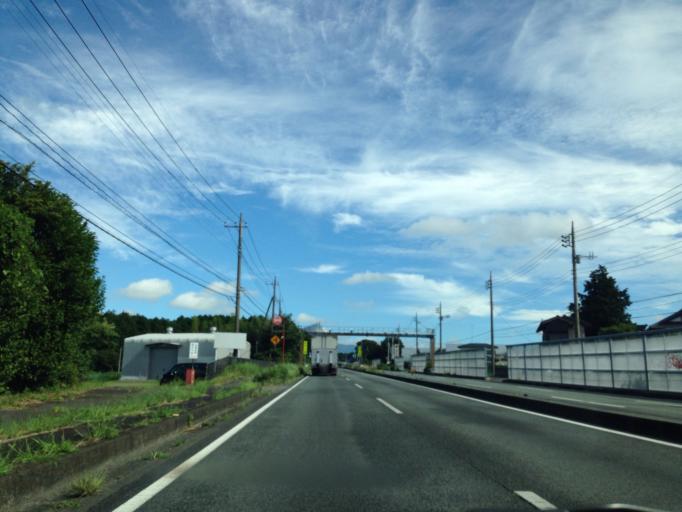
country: JP
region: Shizuoka
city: Gotemba
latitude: 35.2683
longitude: 138.9126
